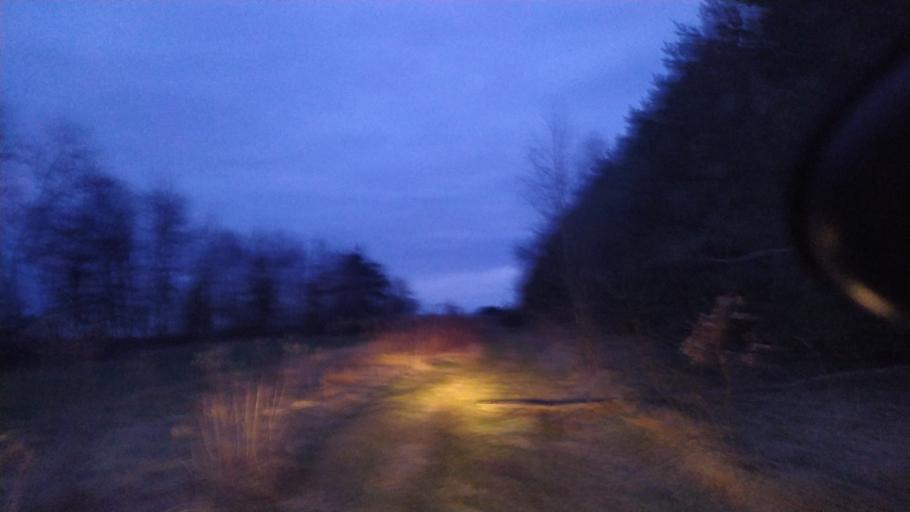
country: PL
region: Lublin Voivodeship
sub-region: Powiat lubelski
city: Jastkow
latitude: 51.3827
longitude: 22.4381
